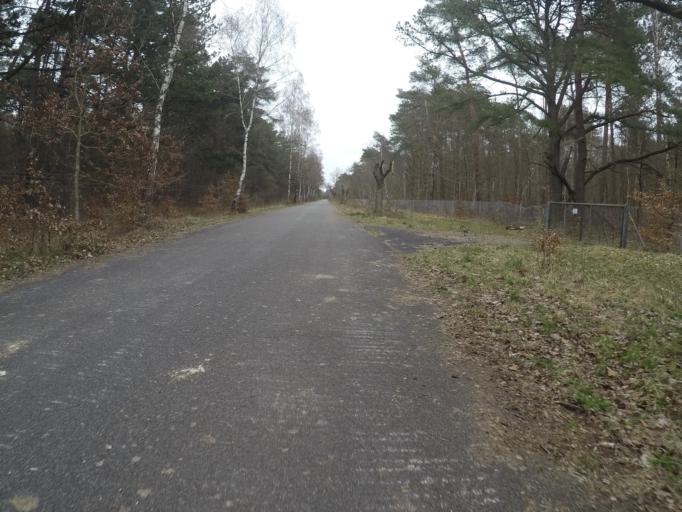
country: DE
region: Lower Saxony
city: Nordholz
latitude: 53.8036
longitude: 8.6351
